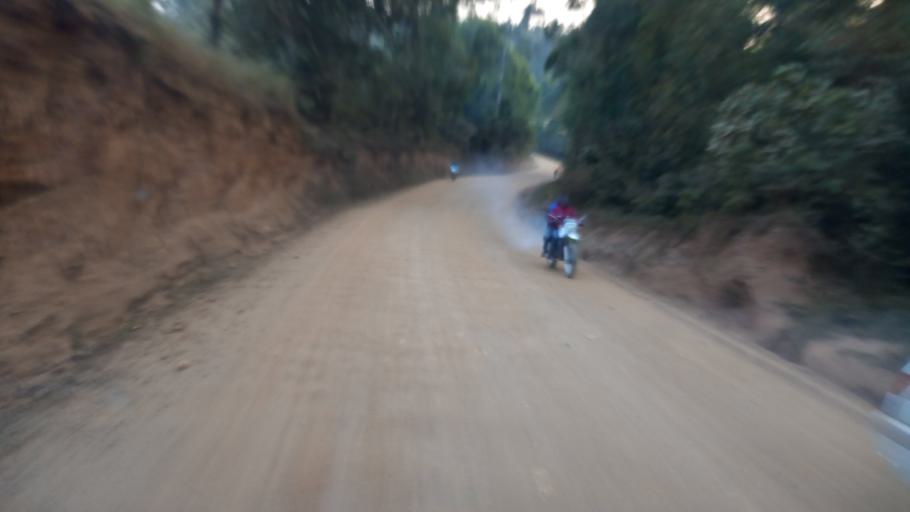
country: UG
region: Western Region
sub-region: Rukungiri District
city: Rukungiri
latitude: -0.7744
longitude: 29.9263
